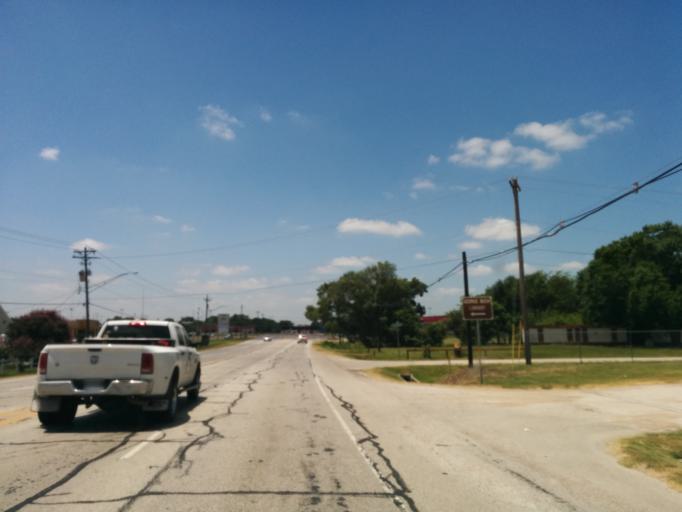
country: US
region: Texas
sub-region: Brazos County
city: Bryan
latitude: 30.6906
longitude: -96.3688
